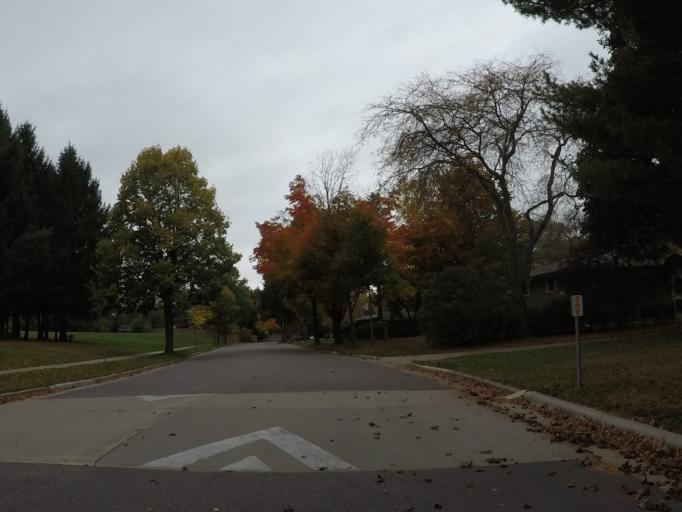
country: US
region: Wisconsin
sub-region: Dane County
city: Shorewood Hills
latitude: 43.0666
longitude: -89.4802
